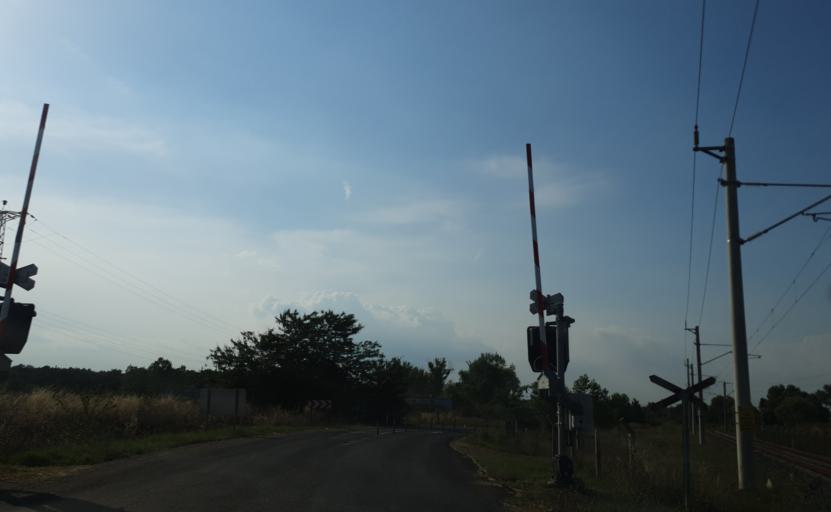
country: TR
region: Tekirdag
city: Muratli
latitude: 41.1828
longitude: 27.4822
